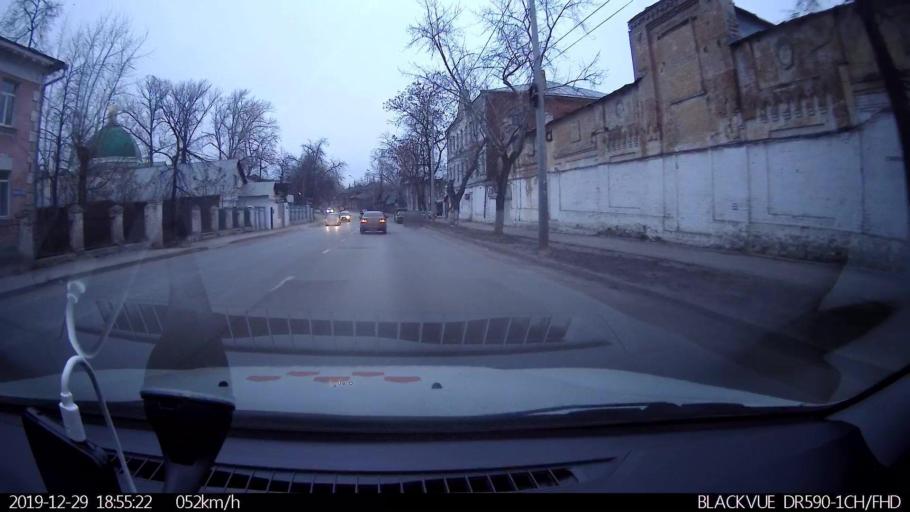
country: RU
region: Nizjnij Novgorod
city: Nizhniy Novgorod
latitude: 56.3138
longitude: 43.9509
